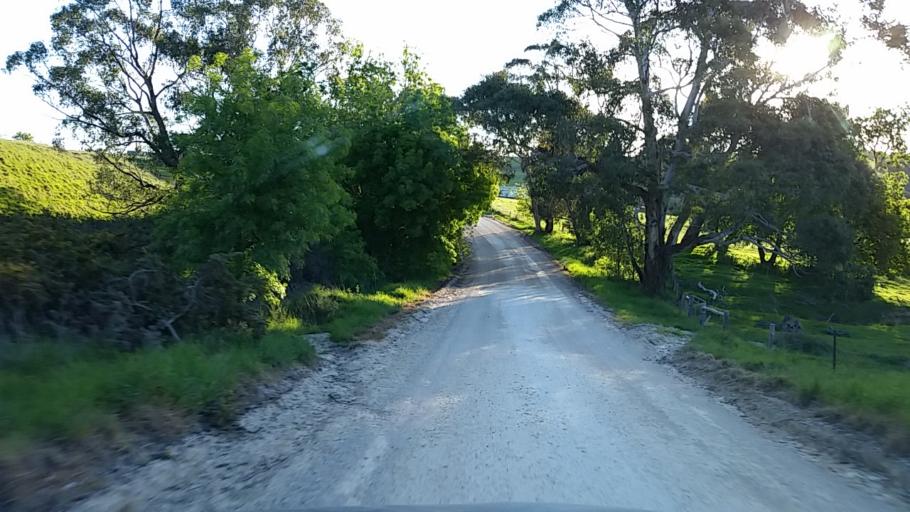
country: AU
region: South Australia
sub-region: Alexandrina
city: Mount Compass
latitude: -35.2846
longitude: 138.6961
